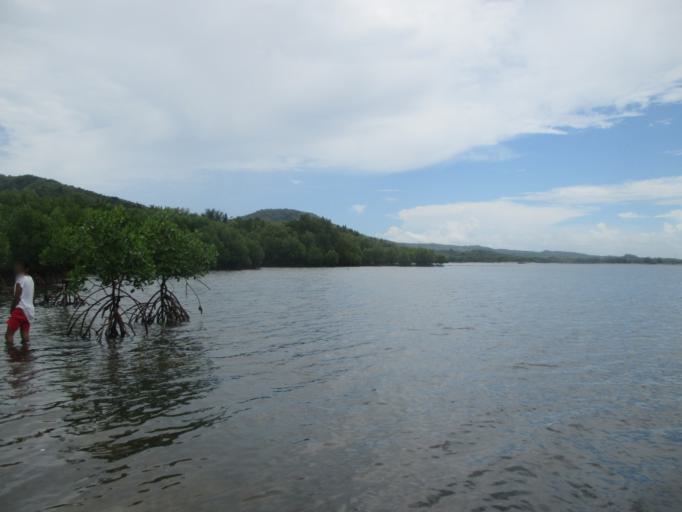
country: PH
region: Calabarzon
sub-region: Province of Batangas
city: Binubusan
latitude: 13.9943
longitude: 120.6240
